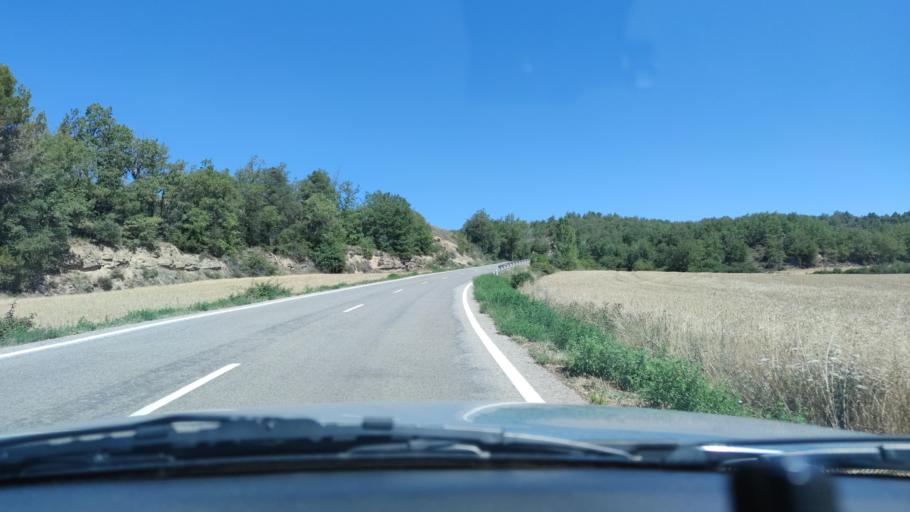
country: ES
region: Catalonia
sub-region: Provincia de Lleida
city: Solsona
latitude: 41.8930
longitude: 1.5619
